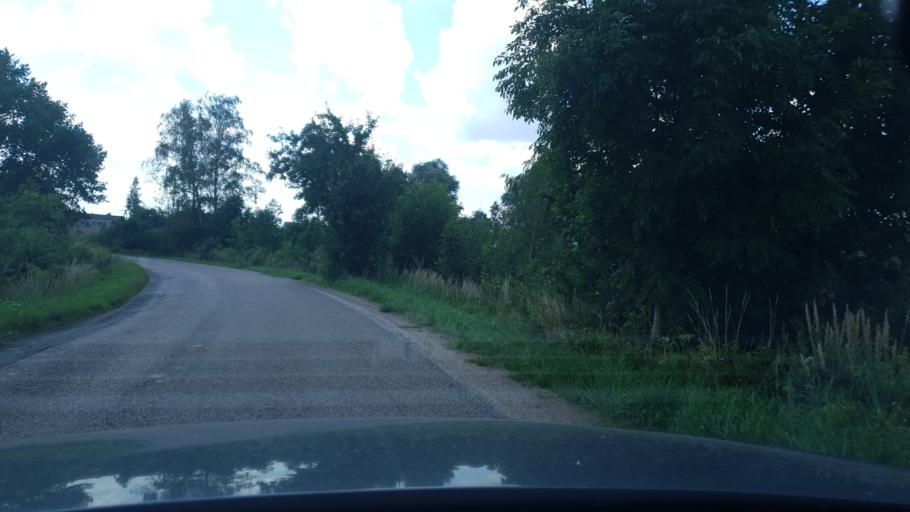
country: PL
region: Kujawsko-Pomorskie
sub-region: Powiat wabrzeski
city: Pluznica
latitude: 53.2787
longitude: 18.8329
